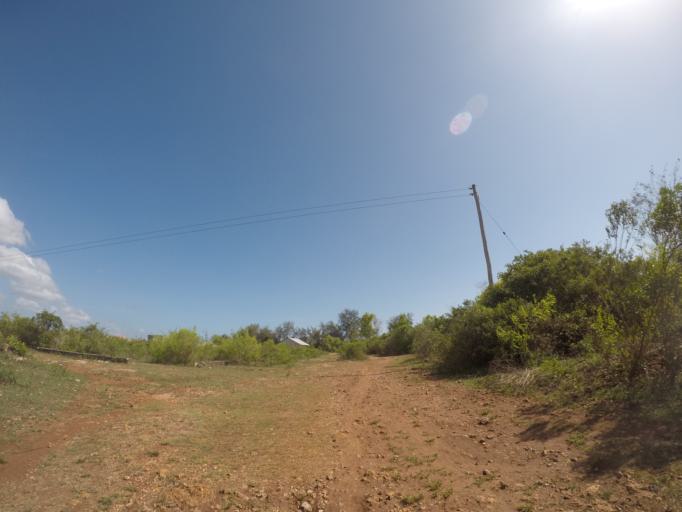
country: TZ
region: Zanzibar Central/South
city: Koani
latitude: -6.2131
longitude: 39.3001
